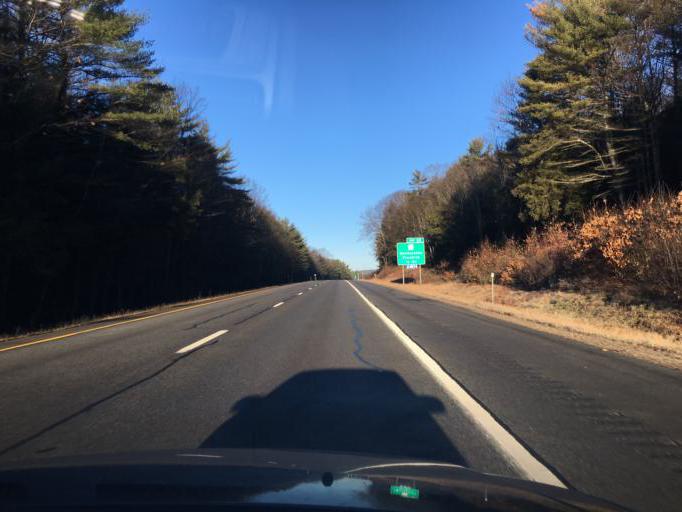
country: US
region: New Hampshire
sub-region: Belknap County
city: Sanbornton
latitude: 43.4990
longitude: -71.6083
